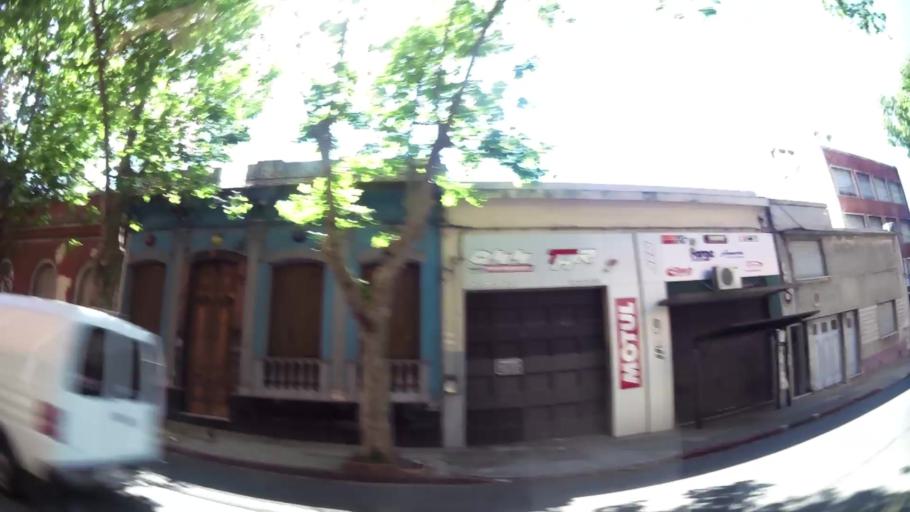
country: UY
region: Montevideo
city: Montevideo
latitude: -34.8949
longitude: -56.1875
